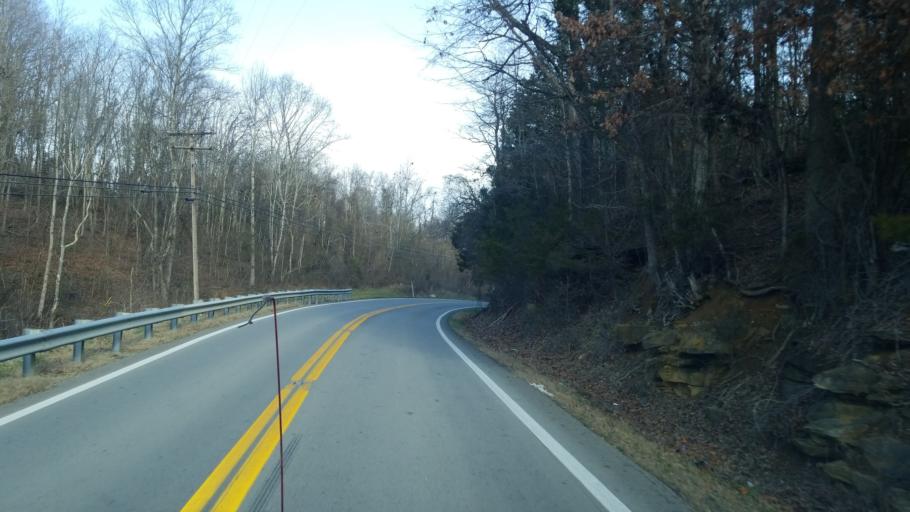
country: US
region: Kentucky
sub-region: Russell County
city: Jamestown
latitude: 36.8953
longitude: -85.0956
